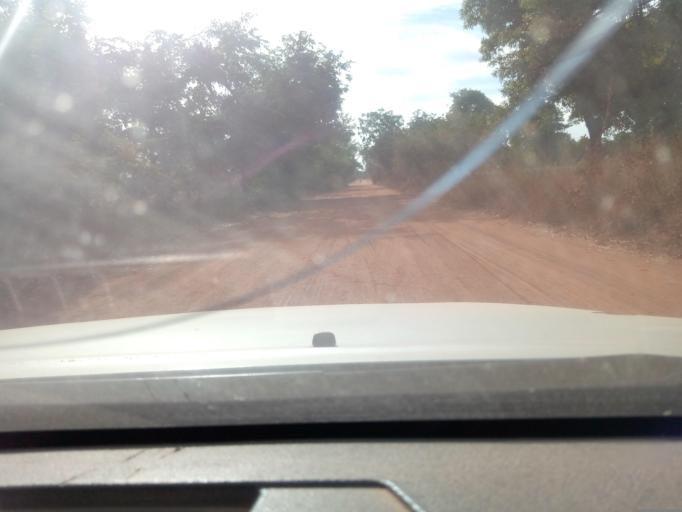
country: ML
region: Sikasso
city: Sikasso
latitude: 11.9354
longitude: -6.0758
